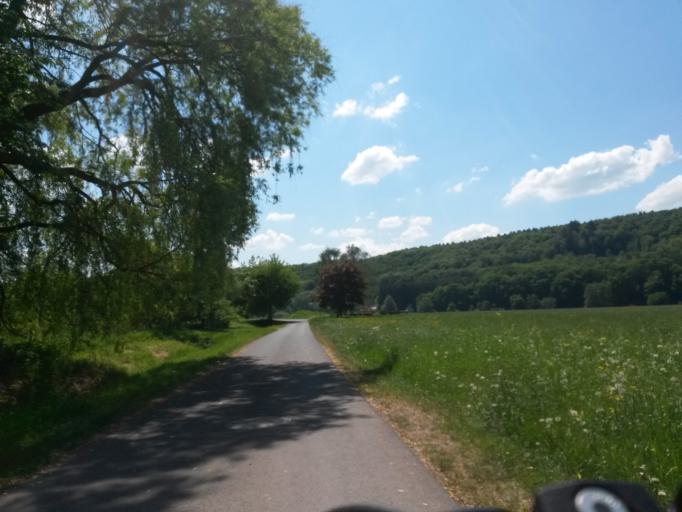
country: DE
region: Bavaria
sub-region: Regierungsbezirk Unterfranken
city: Bad Bocklet
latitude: 50.2468
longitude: 10.0645
